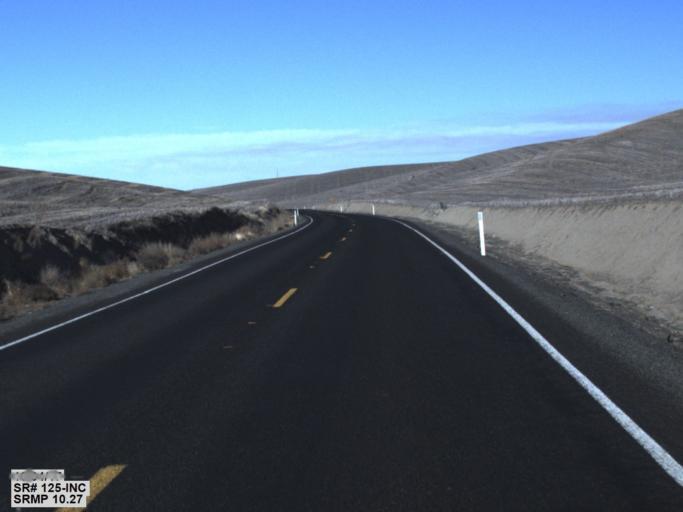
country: US
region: Washington
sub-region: Walla Walla County
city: Walla Walla
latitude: 46.1215
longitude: -118.3722
